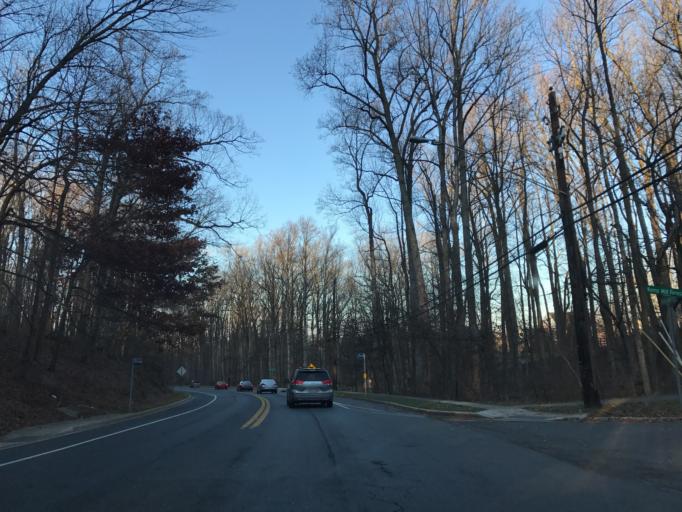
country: US
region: Maryland
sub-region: Montgomery County
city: Kemp Mill
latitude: 39.0554
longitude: -77.0237
